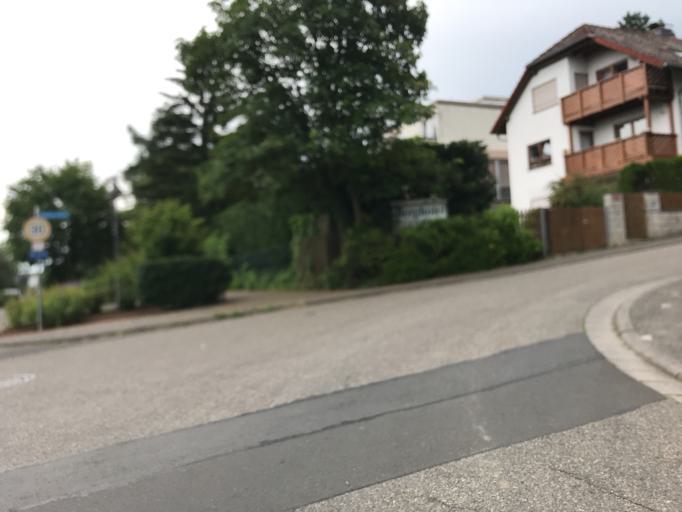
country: DE
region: Rheinland-Pfalz
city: Budenheim
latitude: 50.0190
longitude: 8.1715
